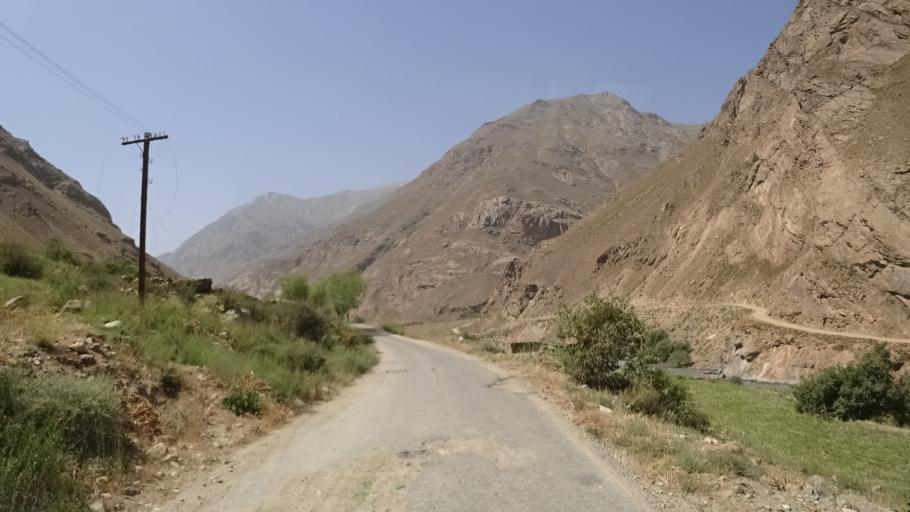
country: TJ
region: Gorno-Badakhshan
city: Khorugh
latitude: 37.1509
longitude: 71.4513
